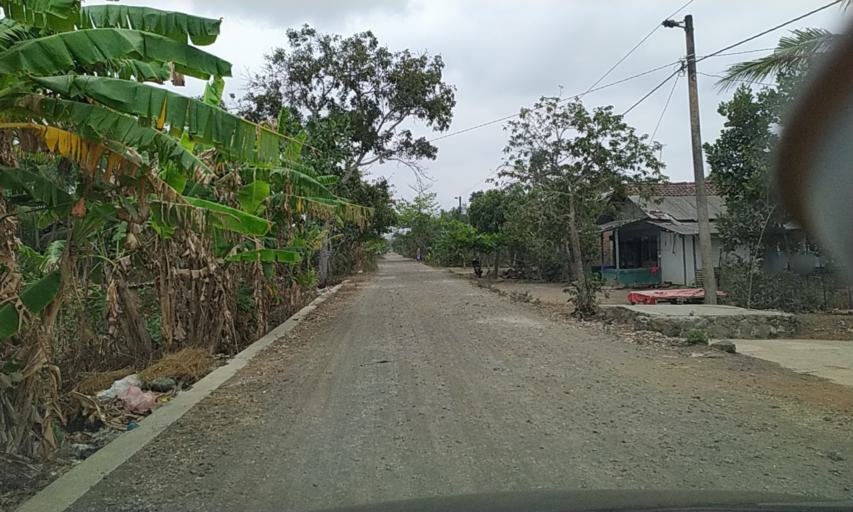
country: ID
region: Central Java
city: Jeruklegi
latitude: -7.6470
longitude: 108.9314
